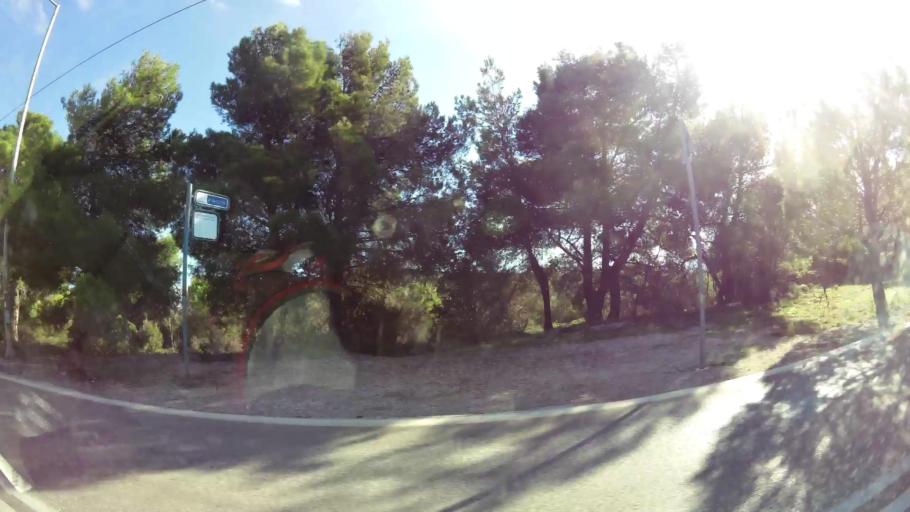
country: GR
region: Attica
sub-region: Nomarchia Anatolikis Attikis
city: Anthousa
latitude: 38.0433
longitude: 23.8863
